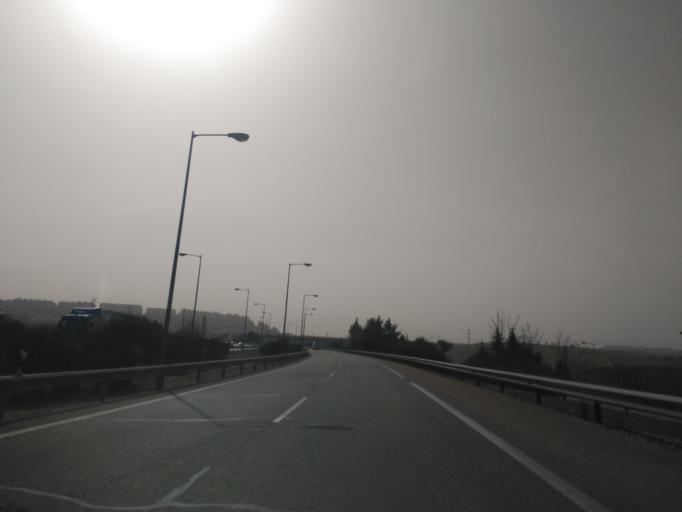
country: ES
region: Castille and Leon
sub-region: Provincia de Valladolid
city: Zaratan
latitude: 41.6555
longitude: -4.7644
